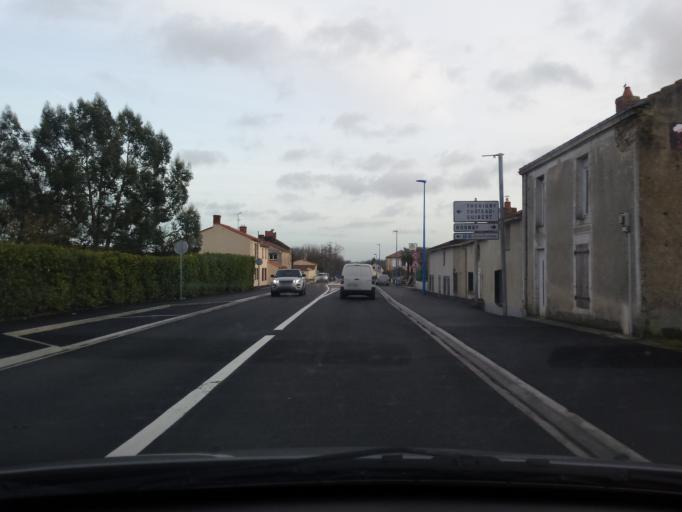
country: FR
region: Pays de la Loire
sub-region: Departement de la Vendee
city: Saint-Florent-des-Bois
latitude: 46.5736
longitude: -1.2847
